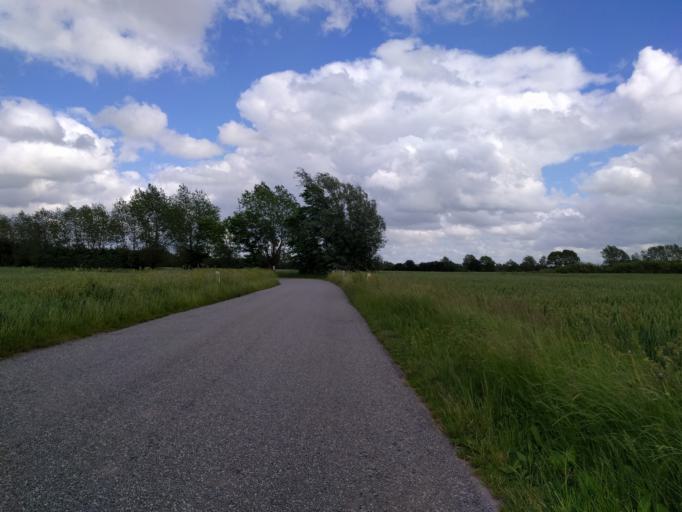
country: DK
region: South Denmark
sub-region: Kerteminde Kommune
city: Munkebo
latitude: 55.4498
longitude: 10.5125
